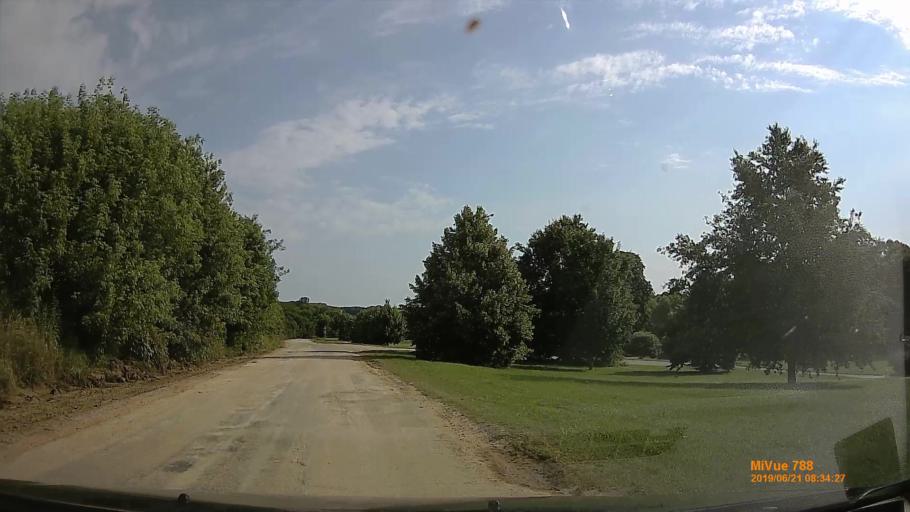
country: HU
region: Baranya
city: Buekkoesd
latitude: 46.1679
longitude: 17.8878
